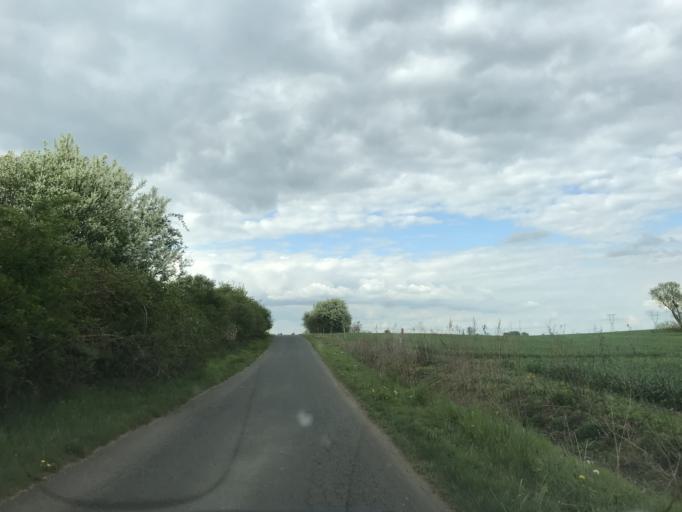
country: PL
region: West Pomeranian Voivodeship
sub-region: Powiat mysliborski
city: Mysliborz
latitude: 52.8766
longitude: 14.8929
